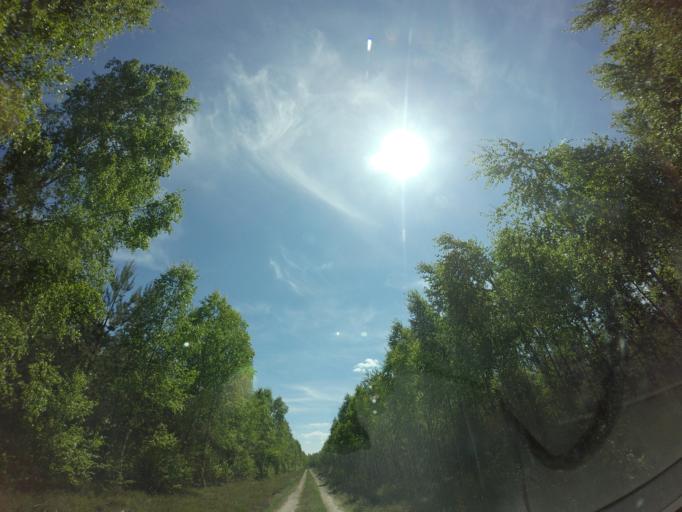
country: PL
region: West Pomeranian Voivodeship
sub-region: Powiat drawski
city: Kalisz Pomorski
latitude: 53.1724
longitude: 15.9027
